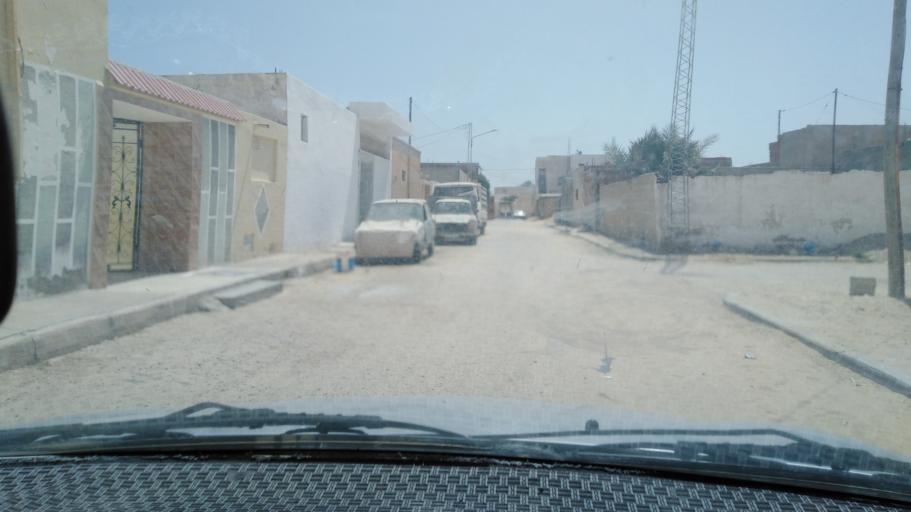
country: TN
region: Qabis
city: Gabes
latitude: 33.9569
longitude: 9.9938
